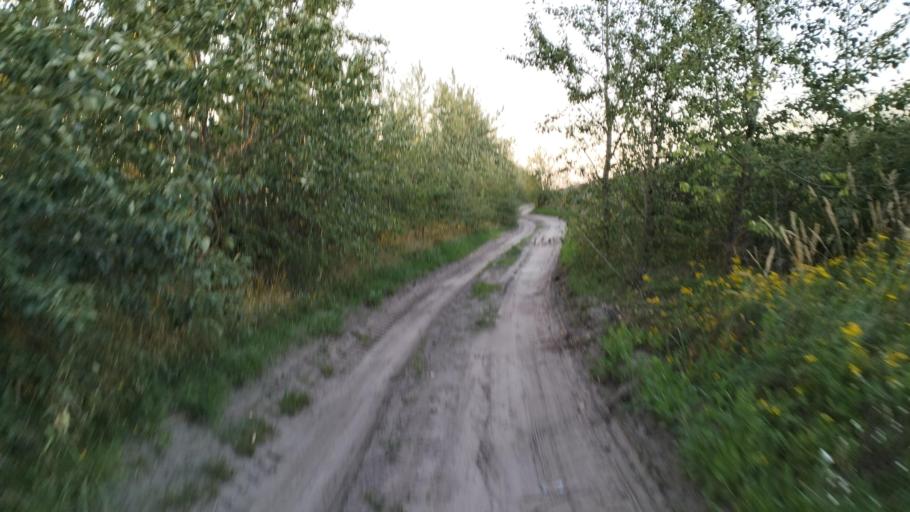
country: BY
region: Brest
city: Davyd-Haradok
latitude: 52.0305
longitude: 27.1941
